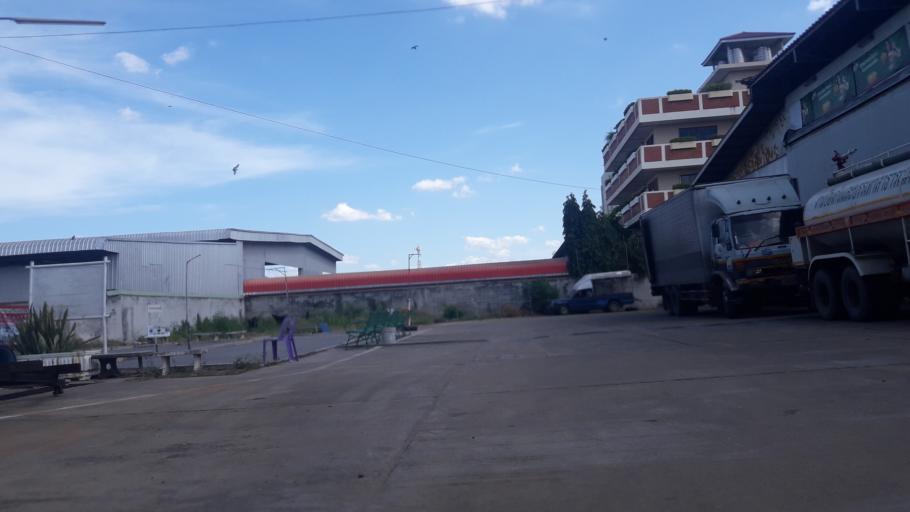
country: TH
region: Phichit
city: Thap Khlo
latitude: 16.1679
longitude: 100.5801
